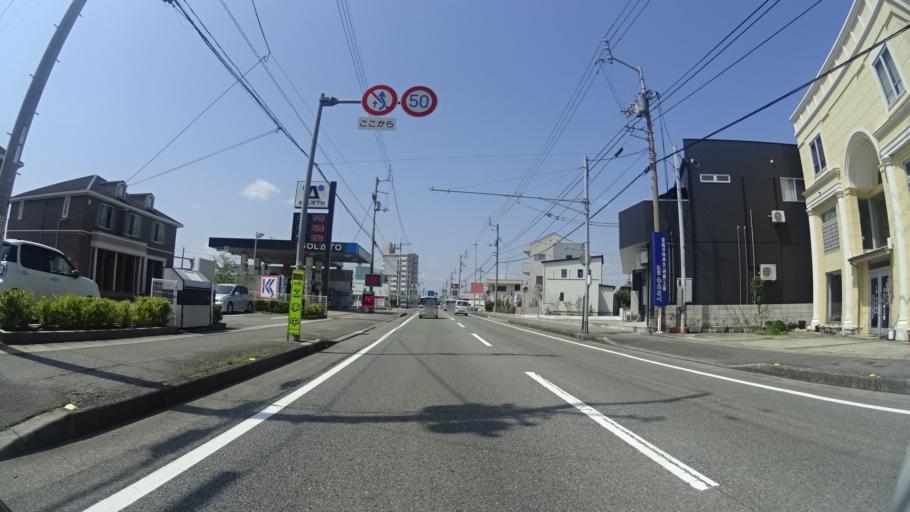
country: JP
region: Tokushima
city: Narutocho-mitsuishi
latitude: 34.1639
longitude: 134.5961
